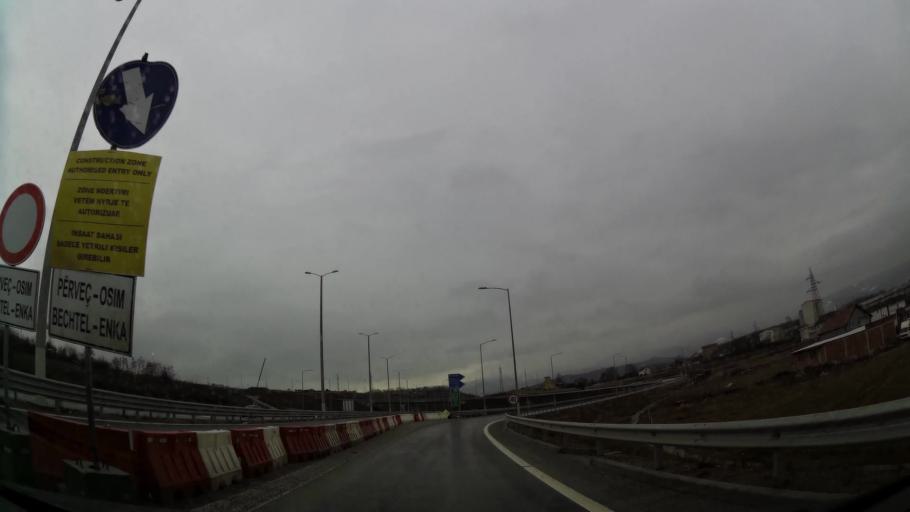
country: XK
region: Ferizaj
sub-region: Komuna e Kacanikut
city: Kacanik
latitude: 42.2782
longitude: 21.2112
